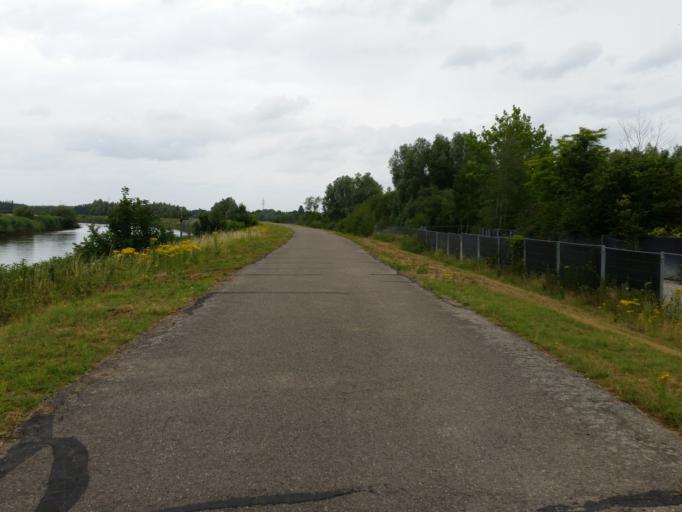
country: BE
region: Flanders
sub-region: Provincie Antwerpen
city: Rumst
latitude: 51.0545
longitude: 4.4428
